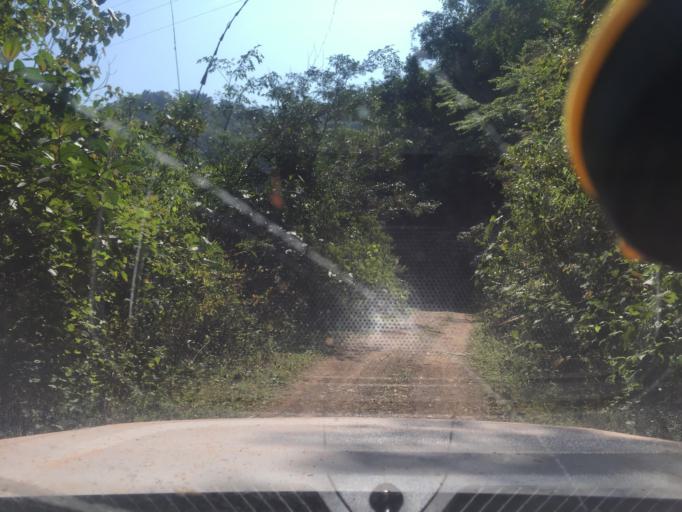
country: LA
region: Phongsali
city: Phongsali
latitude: 21.7054
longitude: 102.3963
